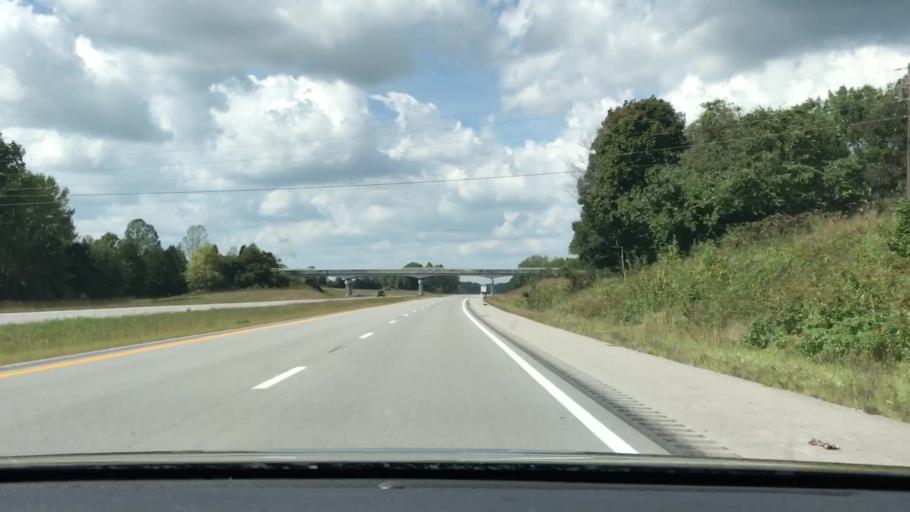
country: US
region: Kentucky
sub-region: Russell County
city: Russell Springs
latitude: 37.0530
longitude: -85.1617
